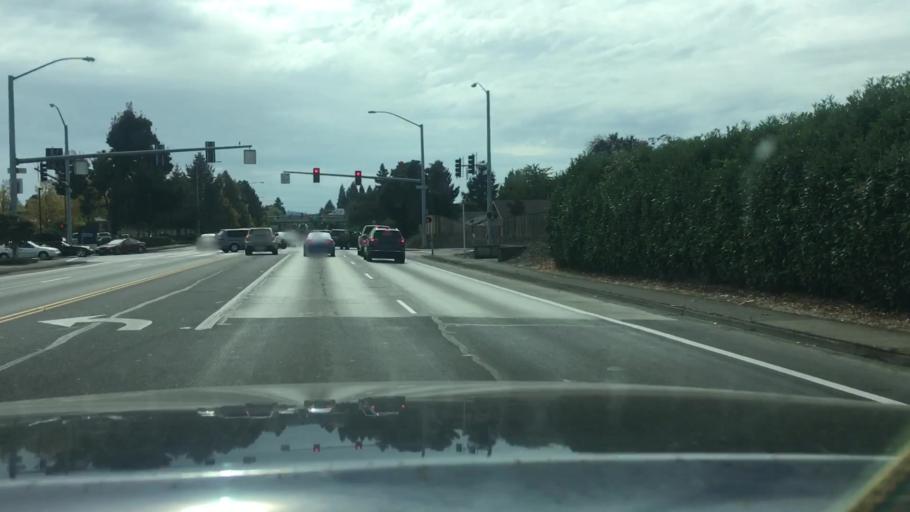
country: US
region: Oregon
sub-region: Lane County
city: Eugene
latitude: 44.0907
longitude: -123.0678
